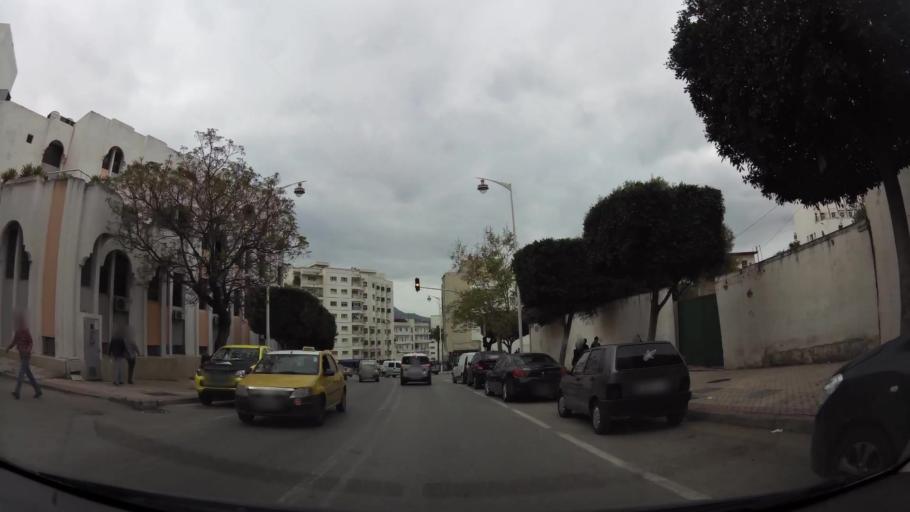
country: MA
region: Tanger-Tetouan
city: Tetouan
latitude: 35.5715
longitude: -5.3863
